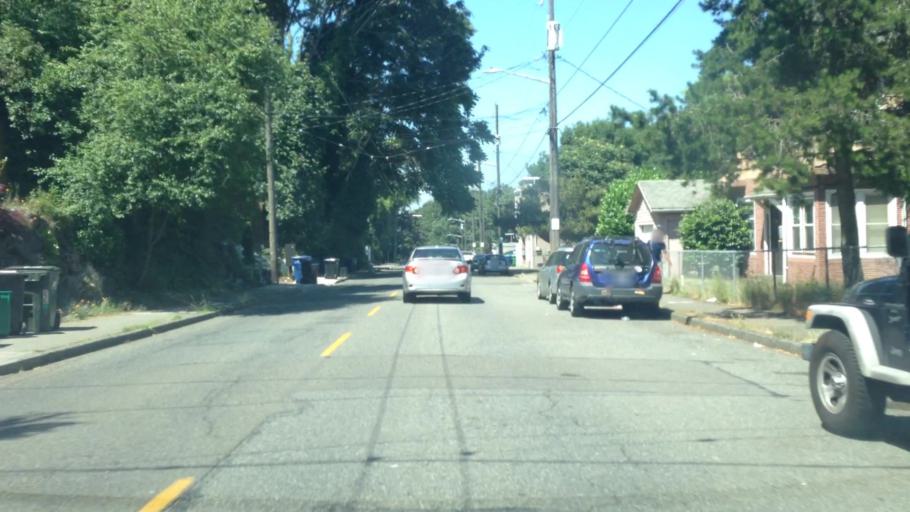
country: US
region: Washington
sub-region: King County
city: Seattle
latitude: 47.5903
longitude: -122.3149
